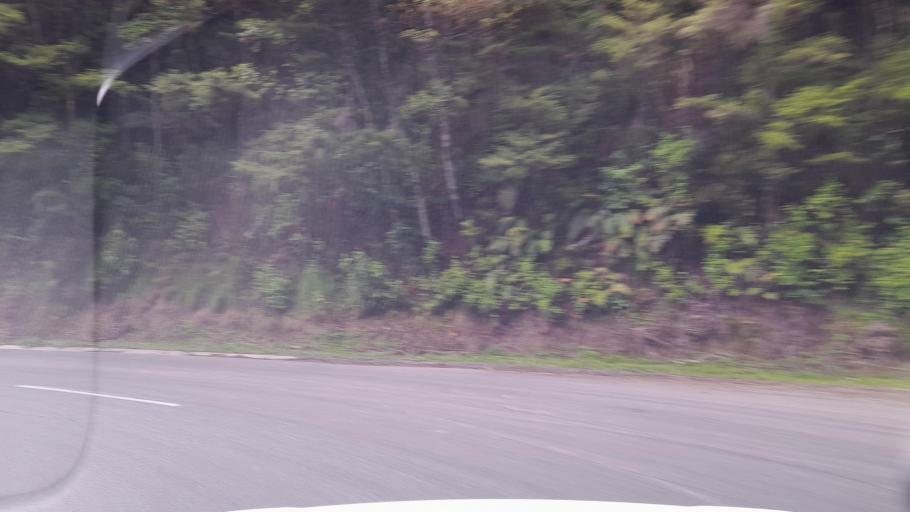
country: NZ
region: Northland
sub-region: Whangarei
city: Maungatapere
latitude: -35.6709
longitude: 174.0405
